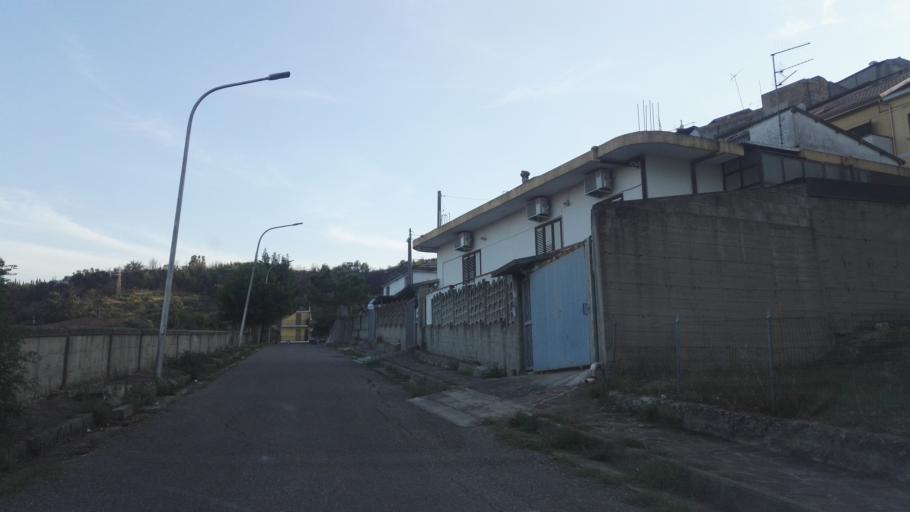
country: IT
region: Calabria
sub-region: Provincia di Reggio Calabria
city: Camini
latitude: 38.4323
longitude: 16.4839
